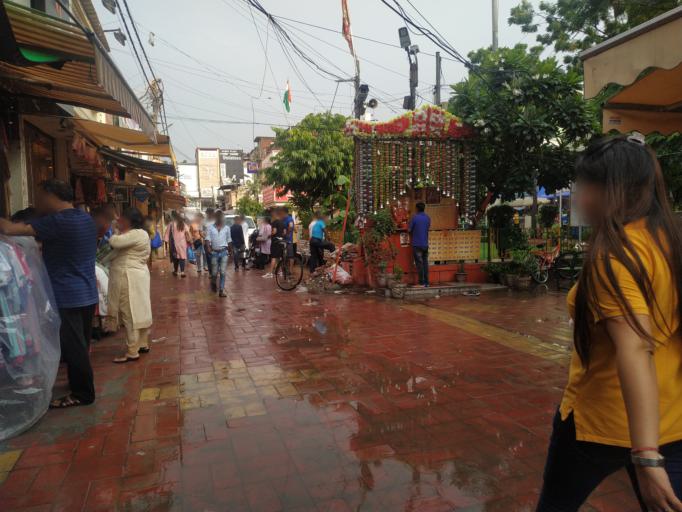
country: IN
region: NCT
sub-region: New Delhi
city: New Delhi
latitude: 28.5695
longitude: 77.2416
